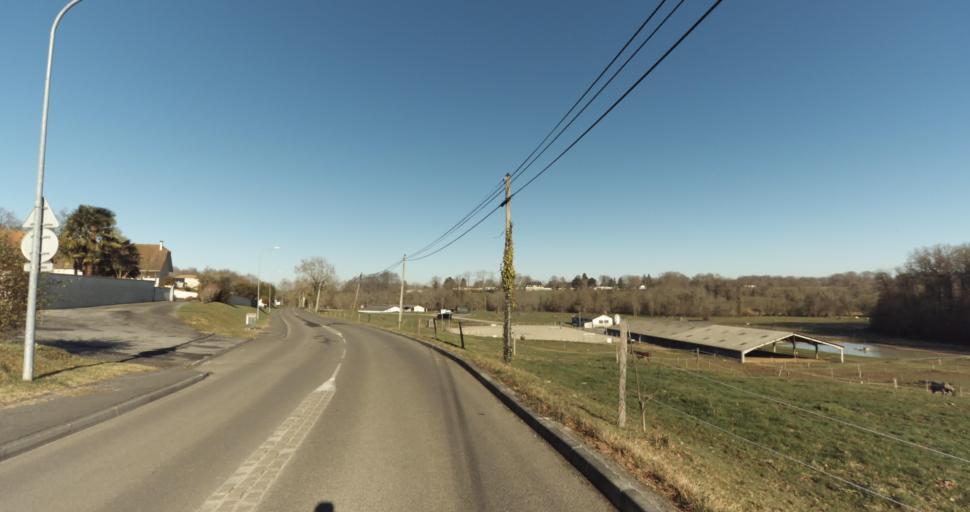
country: FR
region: Aquitaine
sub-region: Departement des Pyrenees-Atlantiques
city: Morlaas
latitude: 43.3552
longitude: -0.2639
